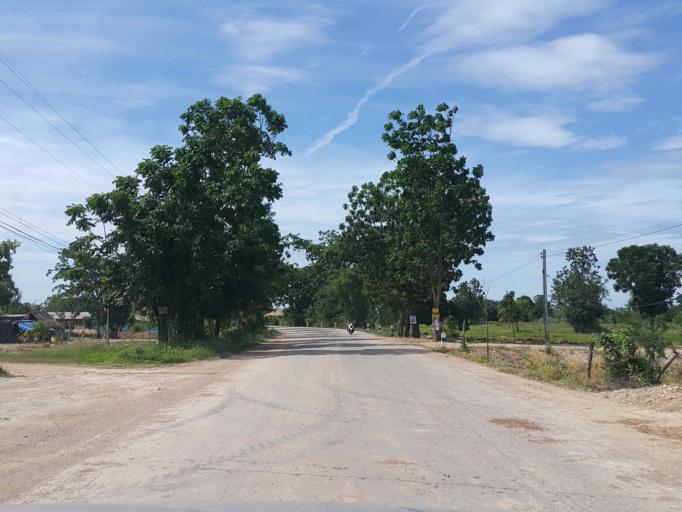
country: TH
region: Sukhothai
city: Ban Dan Lan Hoi
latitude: 17.1487
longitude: 99.5218
